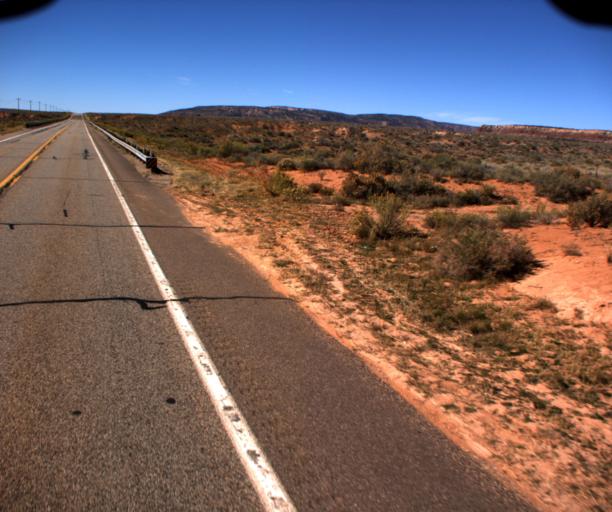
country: US
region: Arizona
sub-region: Coconino County
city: Fredonia
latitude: 36.8789
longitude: -112.6486
